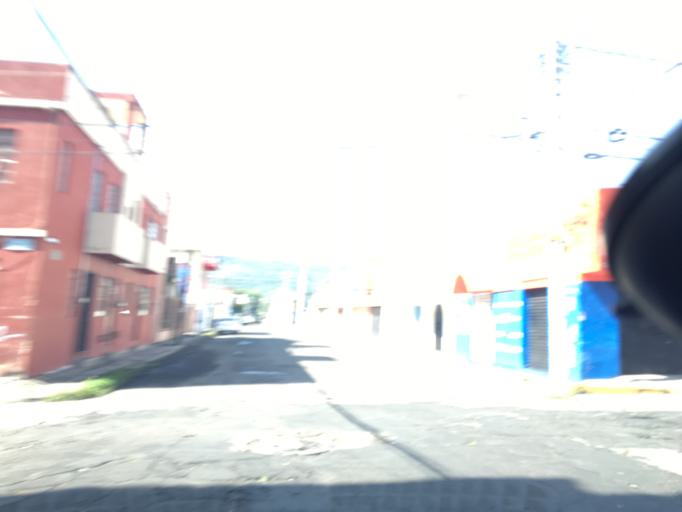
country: MX
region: Michoacan
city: Morelia
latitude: 19.6928
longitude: -101.1696
